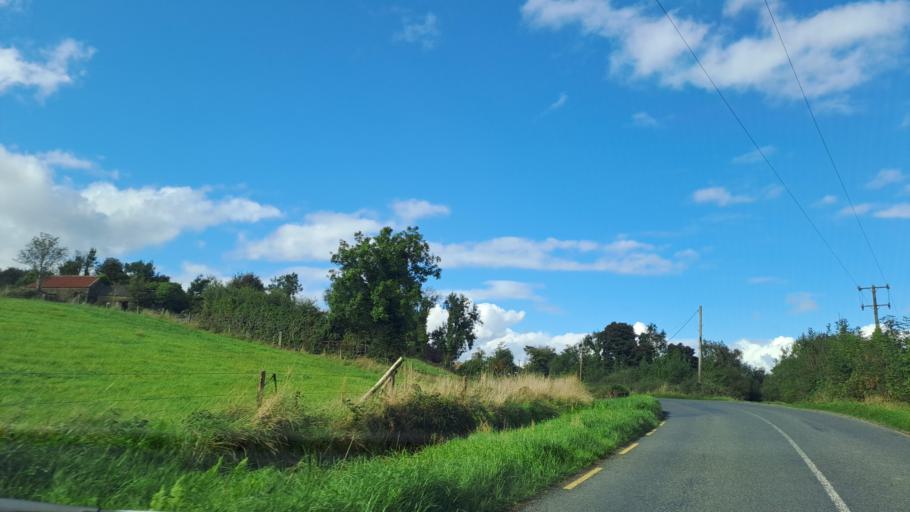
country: IE
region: Ulster
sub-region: An Cabhan
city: Kingscourt
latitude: 53.9553
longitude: -6.8432
